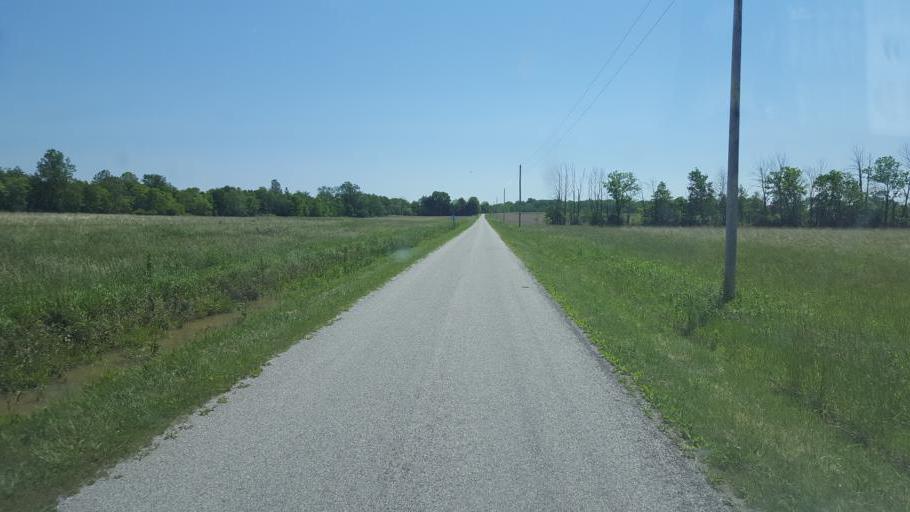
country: US
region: Ohio
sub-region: Hardin County
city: Kenton
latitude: 40.6073
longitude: -83.4192
